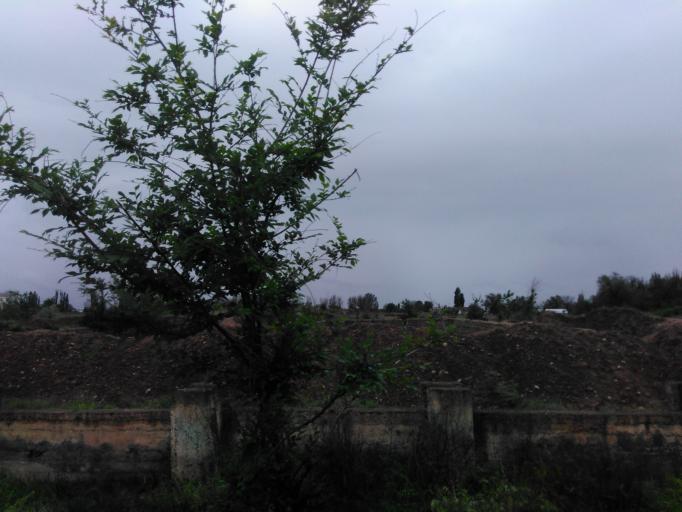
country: KG
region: Chuy
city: Tokmok
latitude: 42.8130
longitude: 75.3303
